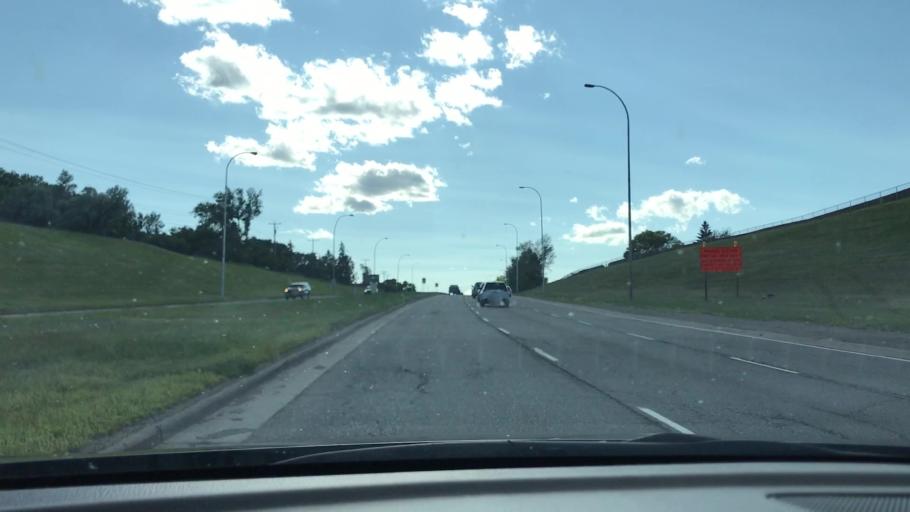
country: CA
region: Alberta
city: Calgary
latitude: 51.0670
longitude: -114.0335
